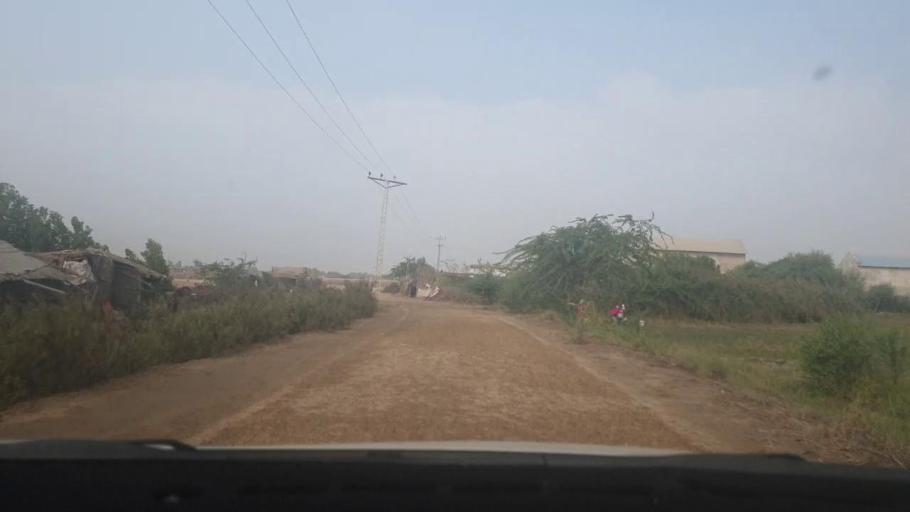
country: PK
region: Sindh
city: Tando Muhammad Khan
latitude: 25.1094
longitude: 68.5382
